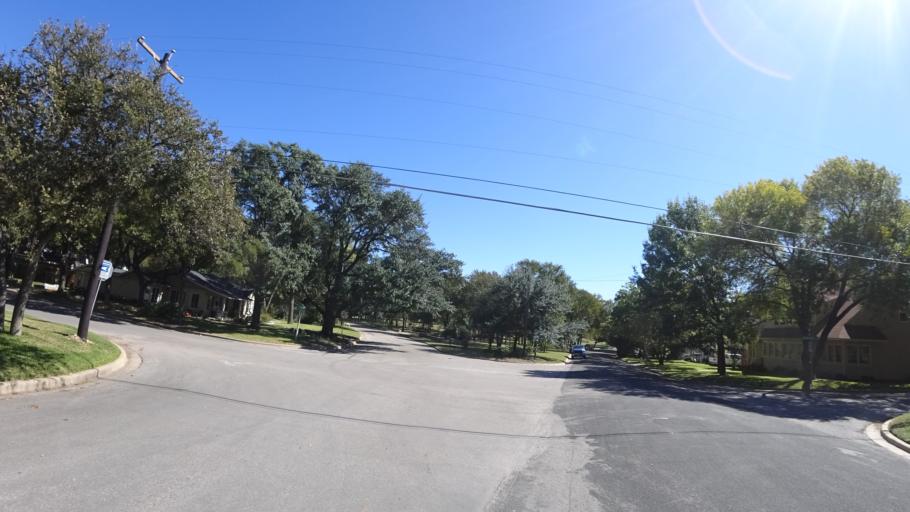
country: US
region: Texas
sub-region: Travis County
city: Austin
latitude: 30.2970
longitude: -97.7614
